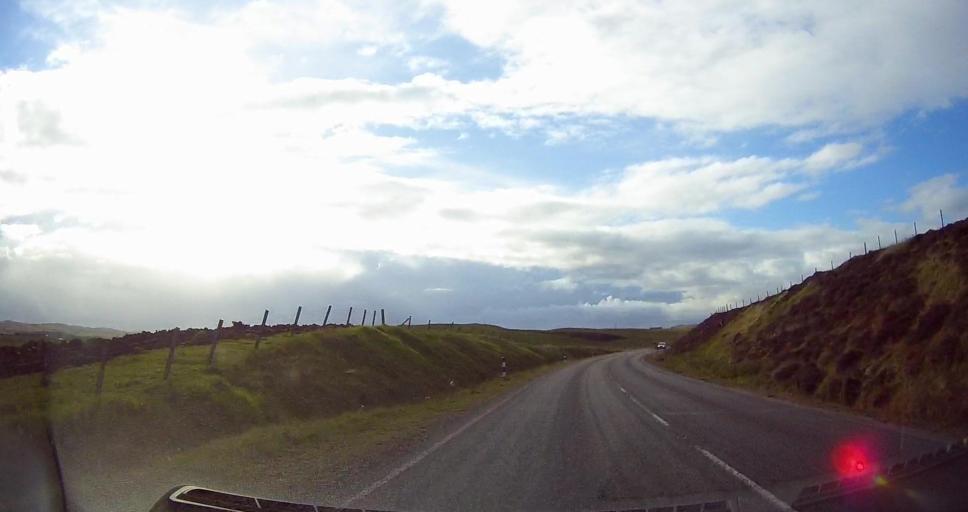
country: GB
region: Scotland
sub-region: Shetland Islands
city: Lerwick
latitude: 60.3718
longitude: -1.3343
